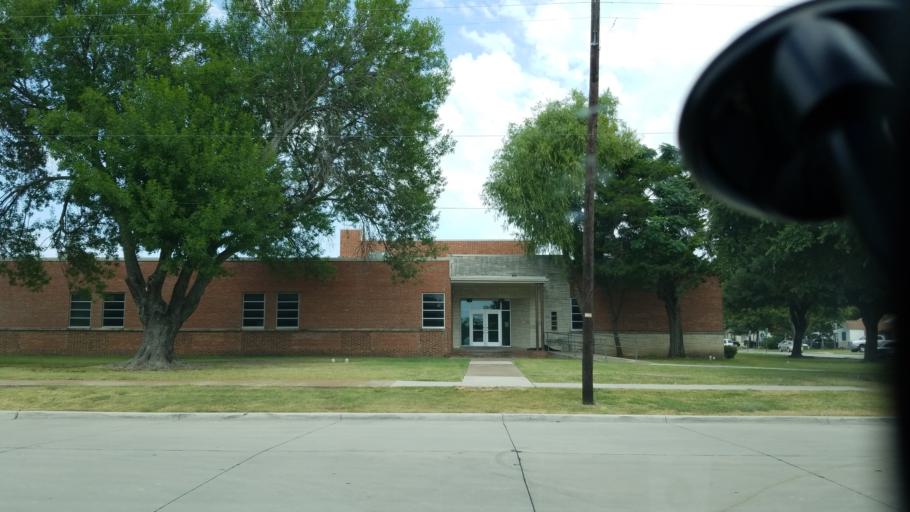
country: US
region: Texas
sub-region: Dallas County
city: Grand Prairie
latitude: 32.7521
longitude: -96.9860
